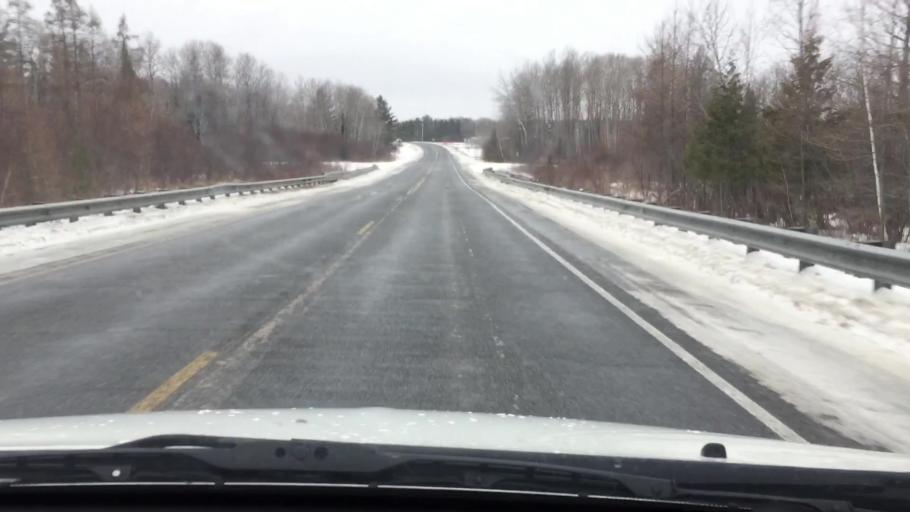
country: US
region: Michigan
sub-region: Wexford County
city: Cadillac
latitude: 44.1180
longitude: -85.4420
